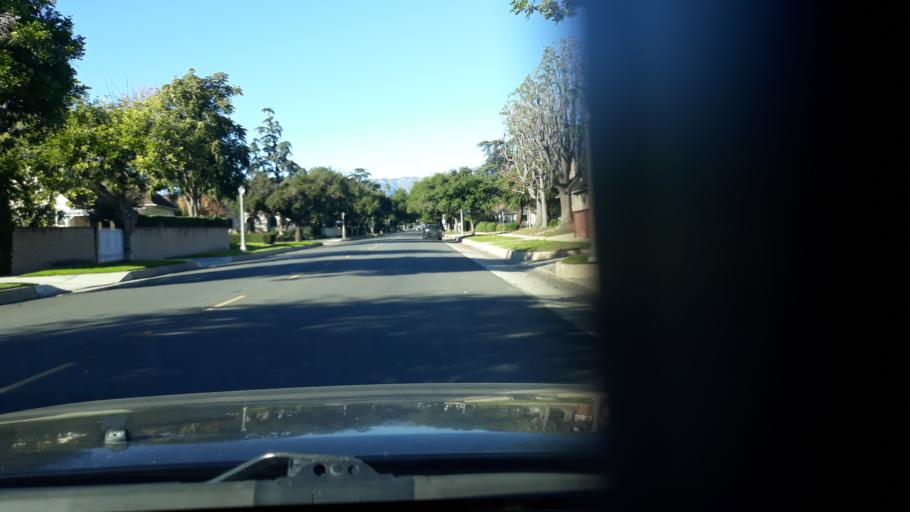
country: US
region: California
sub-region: Los Angeles County
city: San Marino
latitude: 34.1160
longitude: -118.1049
